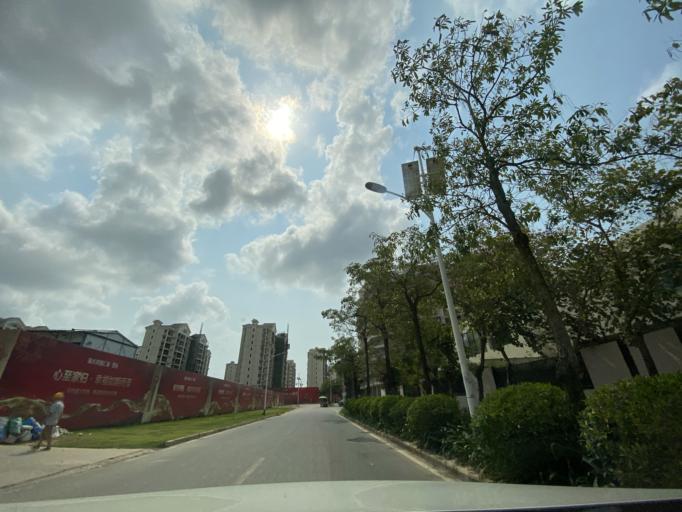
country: CN
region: Hainan
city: Yingzhou
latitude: 18.4090
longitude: 109.8543
